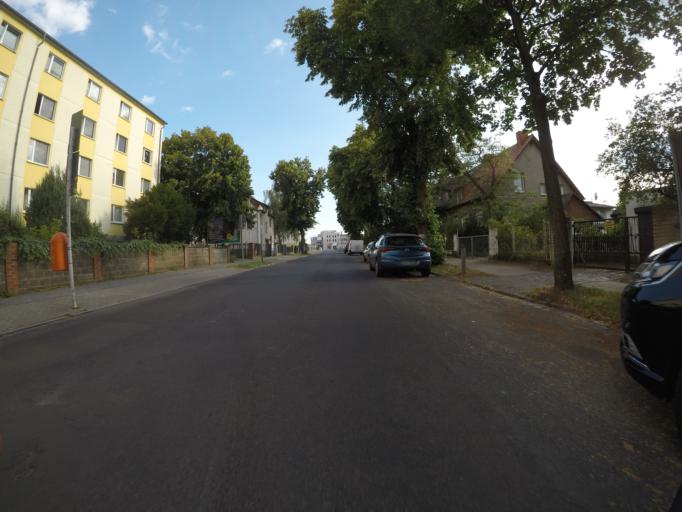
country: DE
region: Berlin
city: Kaulsdorf
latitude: 52.5062
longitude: 13.5914
